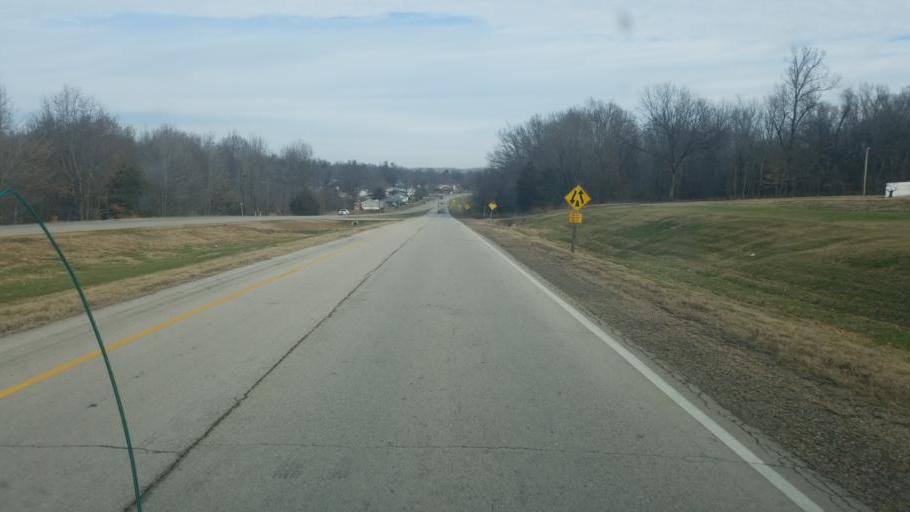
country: US
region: Missouri
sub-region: Stoddard County
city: Bloomfield
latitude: 36.8762
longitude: -89.9280
